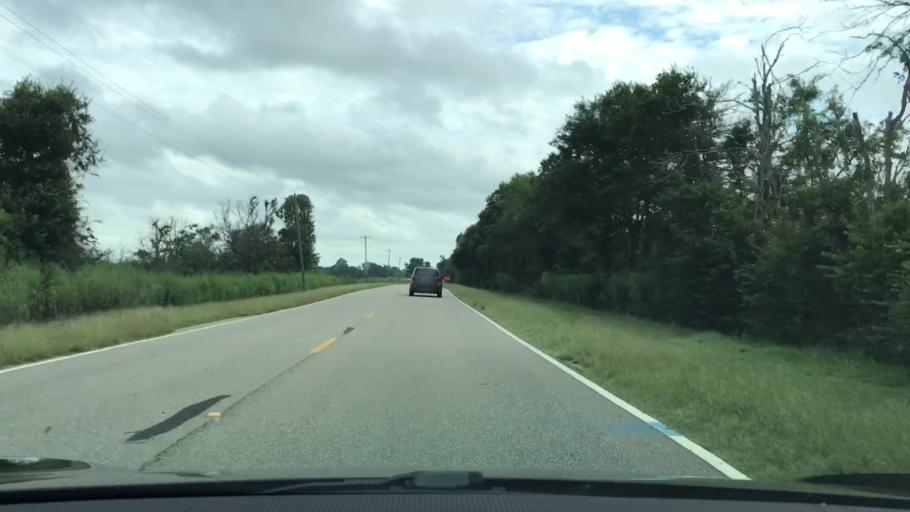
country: US
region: Alabama
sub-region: Montgomery County
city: Pike Road
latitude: 32.2955
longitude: -86.0739
